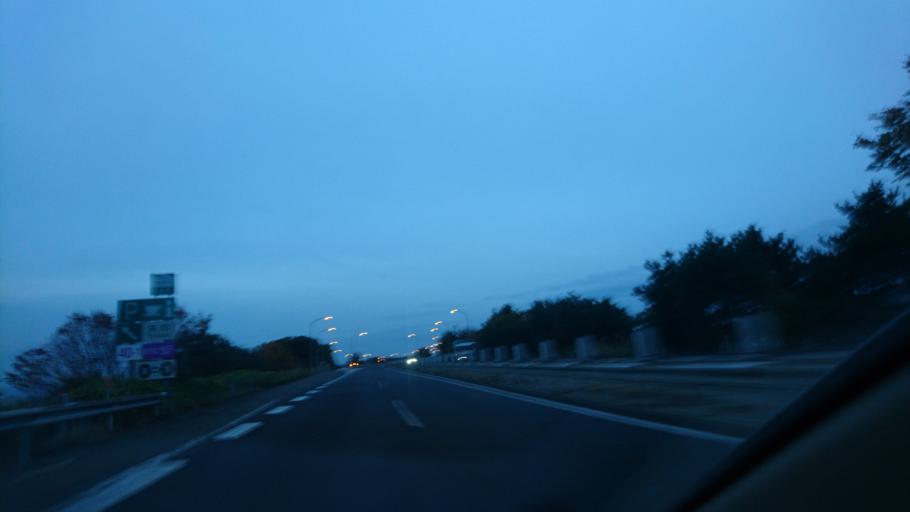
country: JP
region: Iwate
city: Morioka-shi
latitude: 39.6228
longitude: 141.1294
